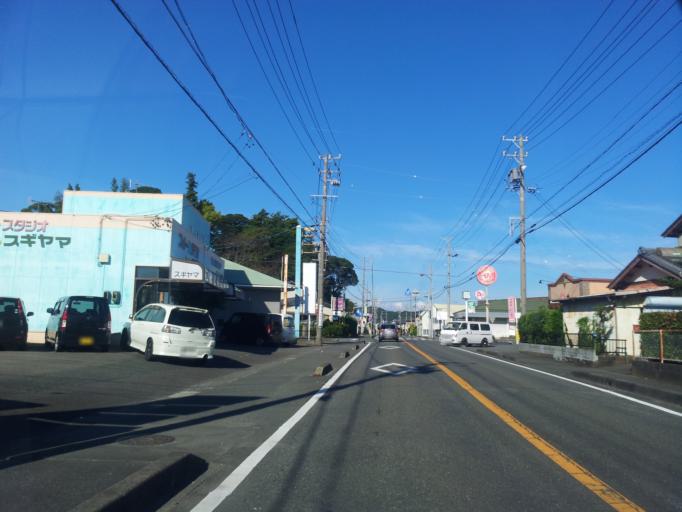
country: JP
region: Shizuoka
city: Sagara
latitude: 34.6891
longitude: 138.1922
